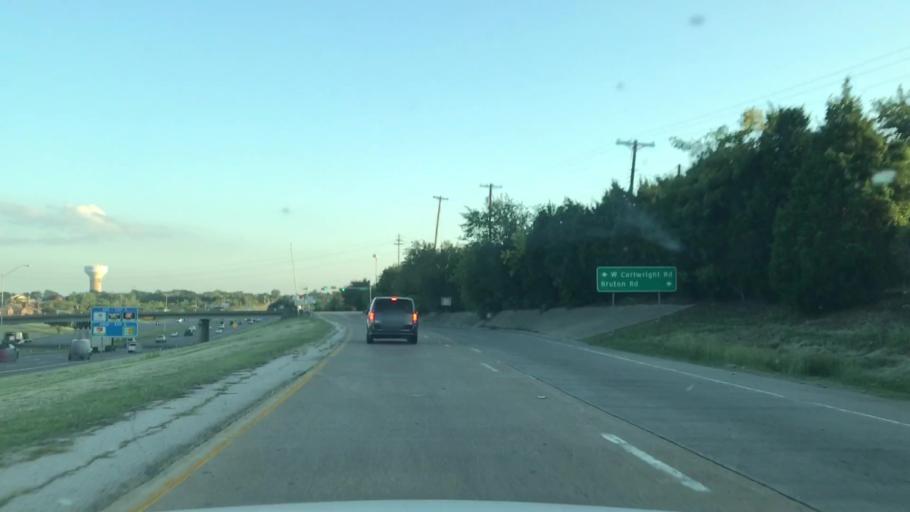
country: US
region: Texas
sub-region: Dallas County
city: Balch Springs
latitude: 32.7502
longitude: -96.6151
